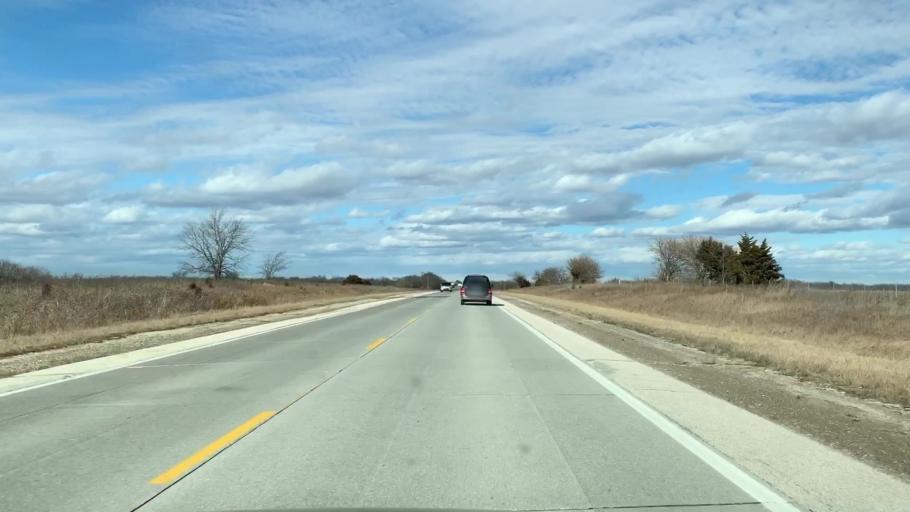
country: US
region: Kansas
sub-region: Neosho County
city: Chanute
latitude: 37.6102
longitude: -95.4795
